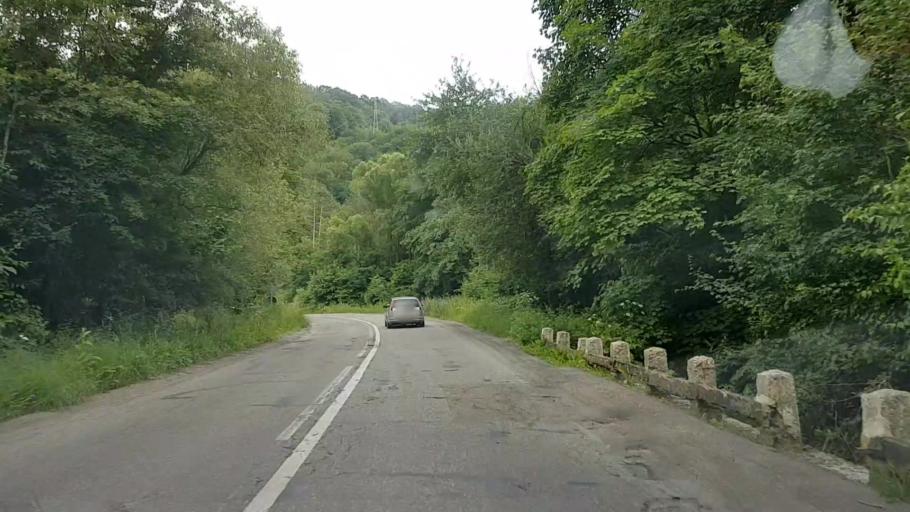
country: RO
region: Neamt
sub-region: Comuna Pangarati
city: Pangarati
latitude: 46.9487
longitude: 26.1298
